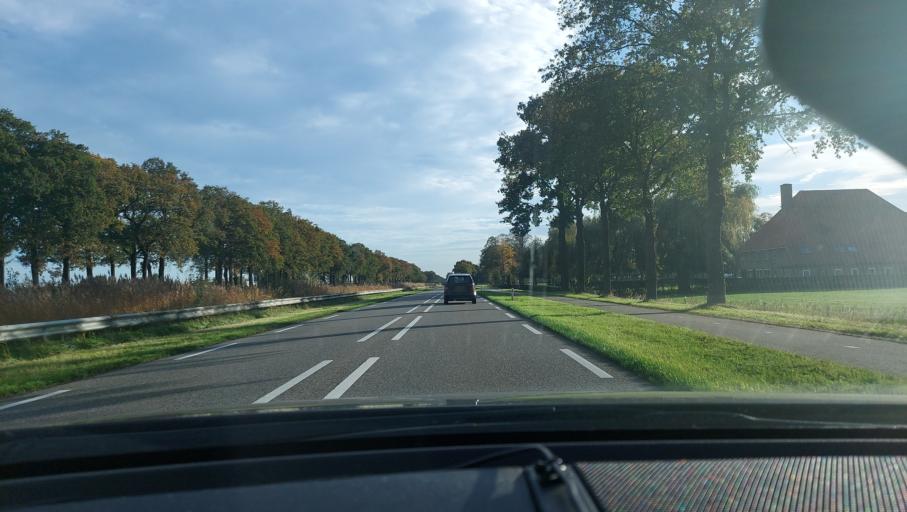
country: NL
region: Limburg
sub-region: Gemeente Nederweert
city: Nederweert
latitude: 51.3126
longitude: 5.7494
